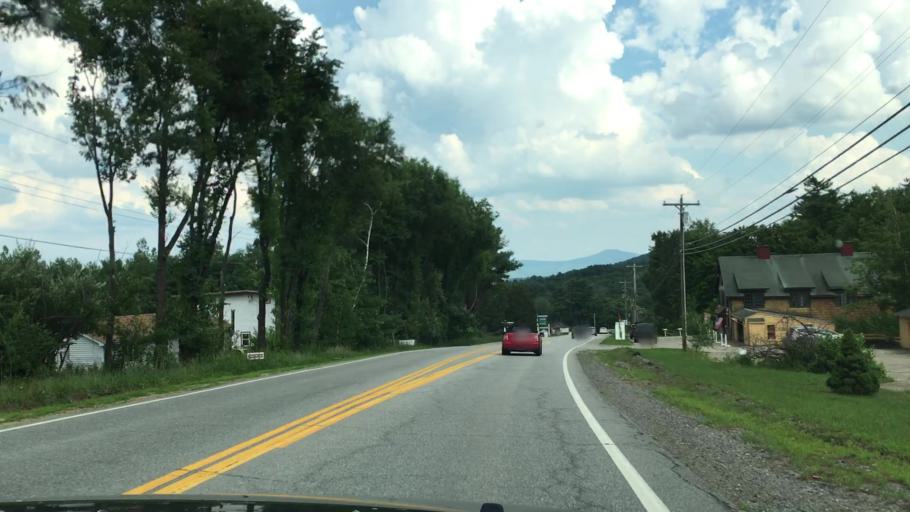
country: US
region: New Hampshire
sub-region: Belknap County
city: Meredith
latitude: 43.6358
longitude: -71.4902
